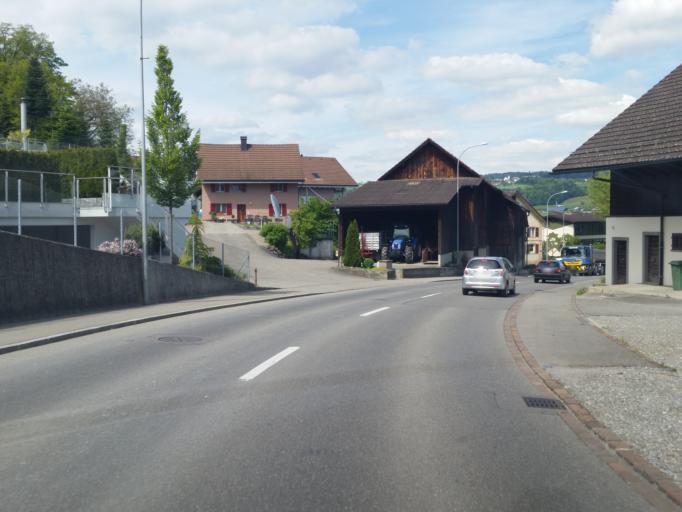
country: CH
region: Aargau
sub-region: Bezirk Bremgarten
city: Unterlunkhofen
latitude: 47.3129
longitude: 8.3610
